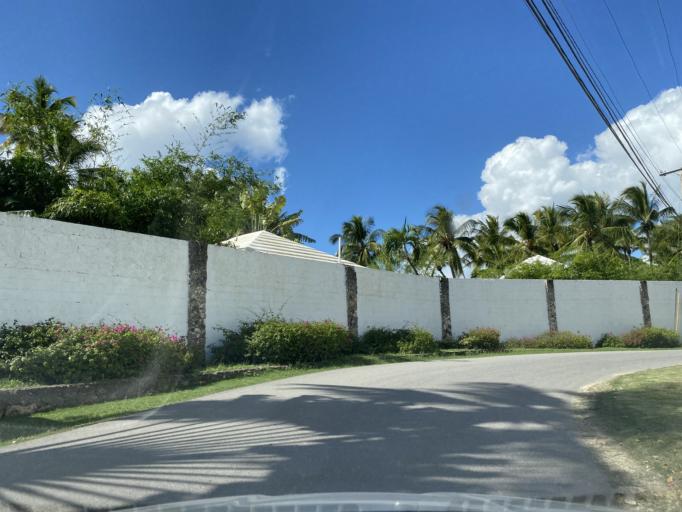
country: DO
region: La Romana
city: La Romana
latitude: 18.3500
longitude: -68.8319
